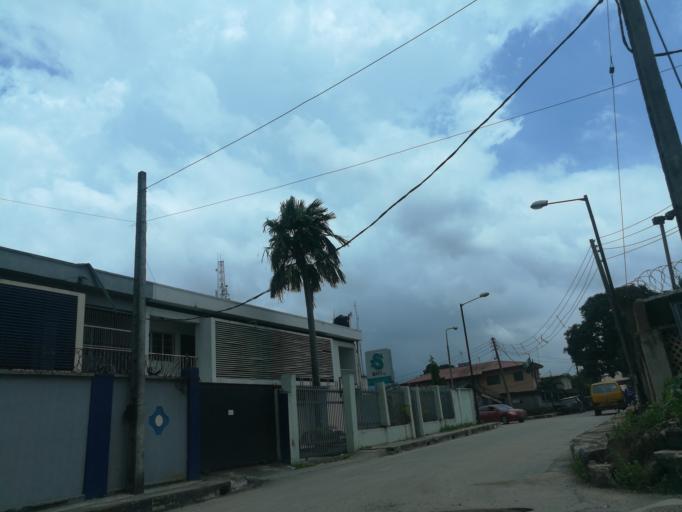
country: NG
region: Lagos
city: Somolu
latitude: 6.5521
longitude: 3.3599
